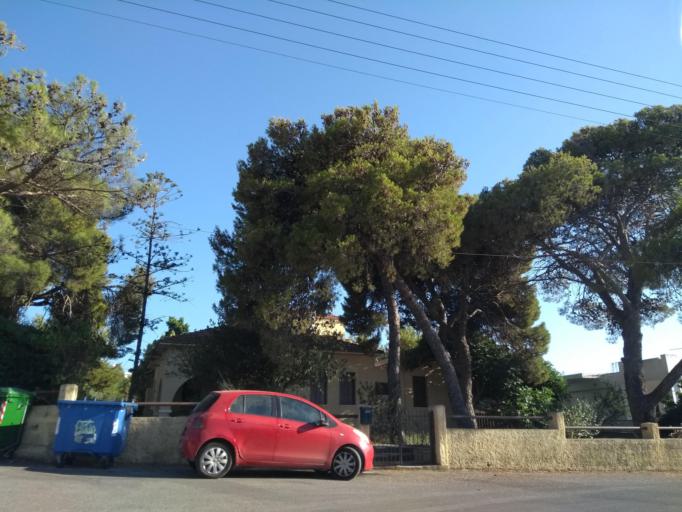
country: GR
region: Crete
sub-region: Nomos Chanias
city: Pithari
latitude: 35.5185
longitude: 24.0765
